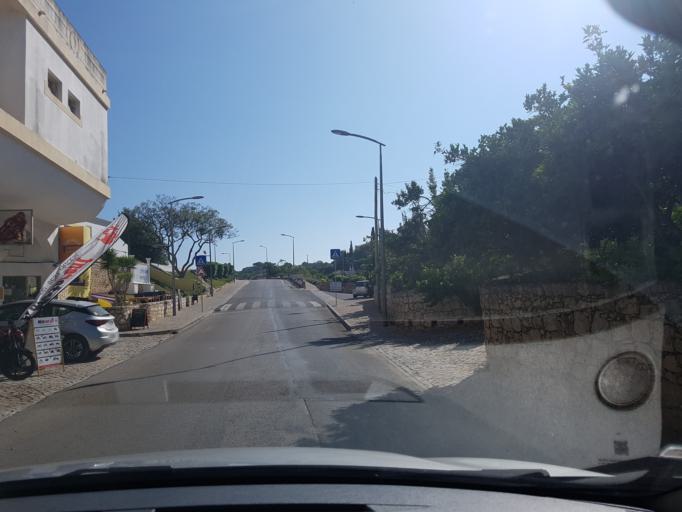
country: PT
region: Faro
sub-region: Lagoa
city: Carvoeiro
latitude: 37.1009
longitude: -8.4671
